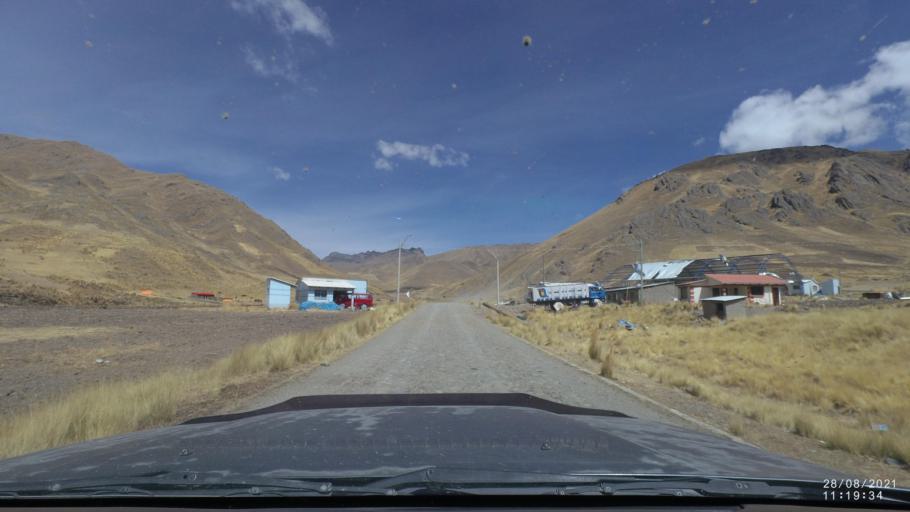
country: BO
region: Cochabamba
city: Cochabamba
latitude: -17.1544
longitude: -66.3338
